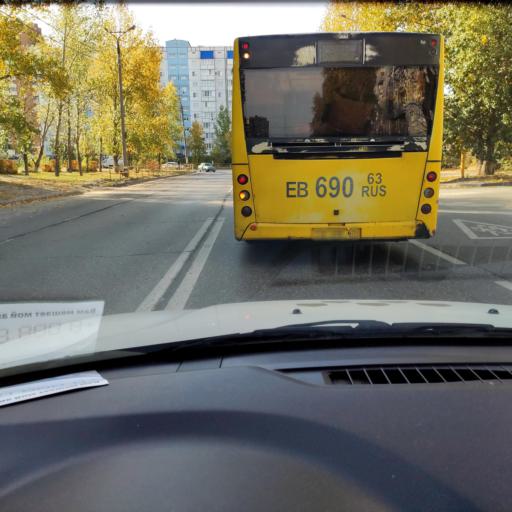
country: RU
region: Samara
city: Zhigulevsk
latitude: 53.4752
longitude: 49.5218
